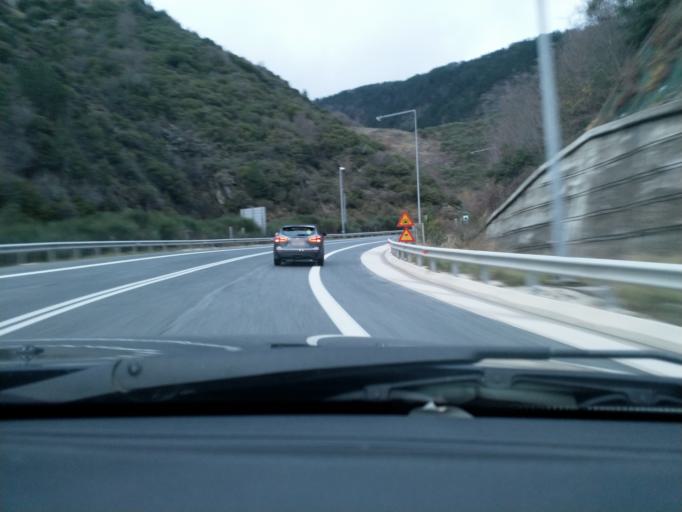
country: GR
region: Epirus
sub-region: Nomos Ioanninon
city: Metsovo
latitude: 39.7631
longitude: 21.1688
